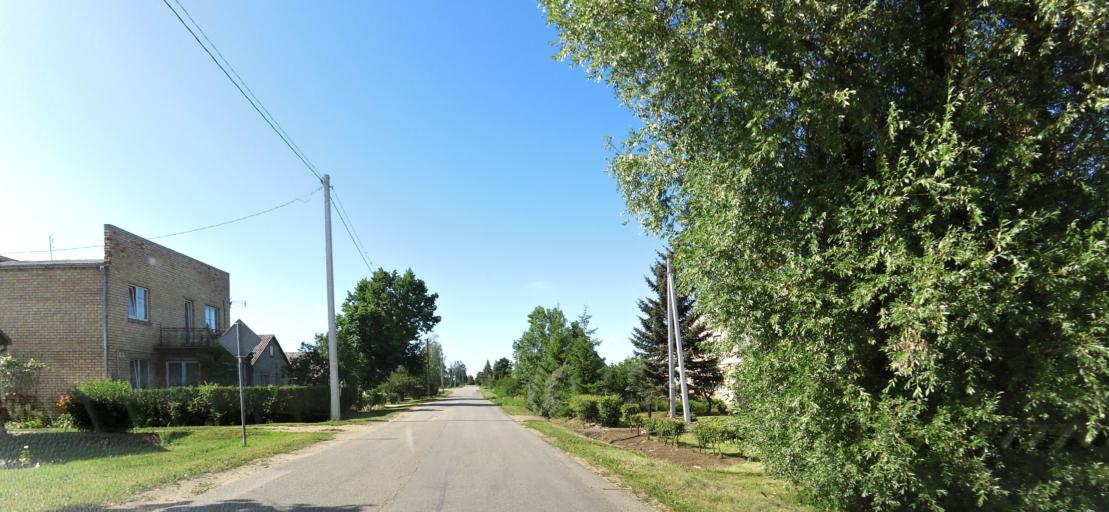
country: LT
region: Panevezys
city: Pasvalys
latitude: 56.1565
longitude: 24.4412
